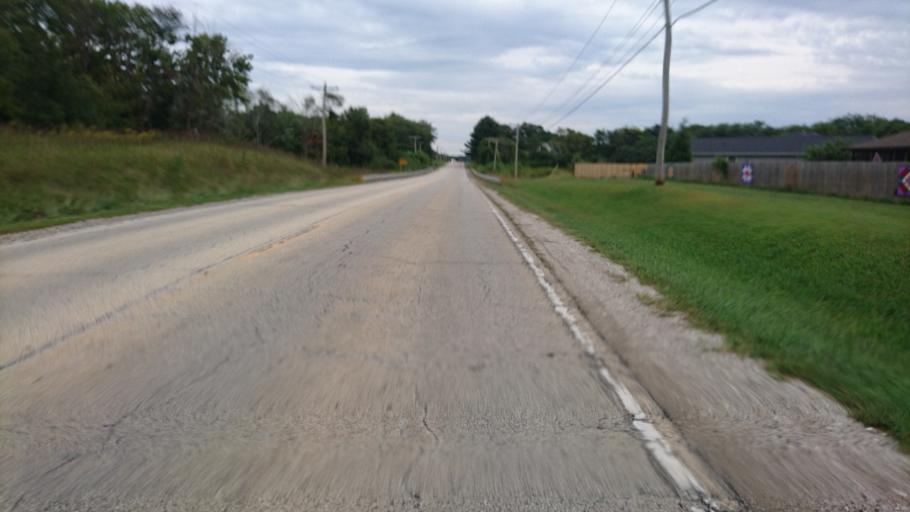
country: US
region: Illinois
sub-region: Sangamon County
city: Chatham
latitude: 39.6768
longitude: -89.6786
